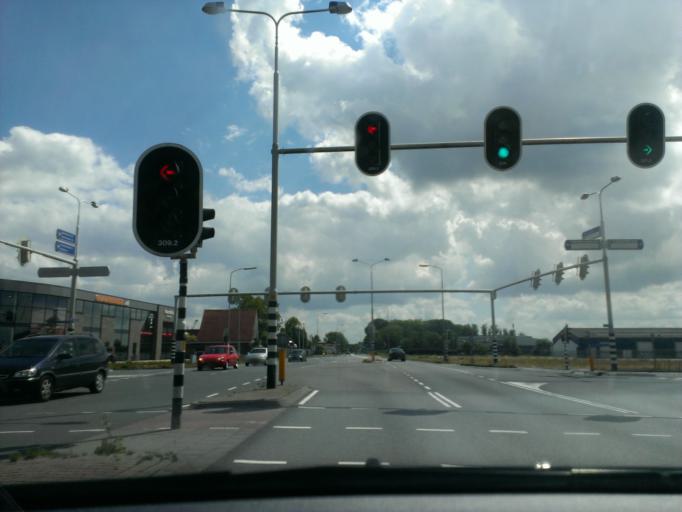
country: NL
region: Gelderland
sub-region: Gemeente Barneveld
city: Voorthuizen
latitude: 52.1659
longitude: 5.5987
